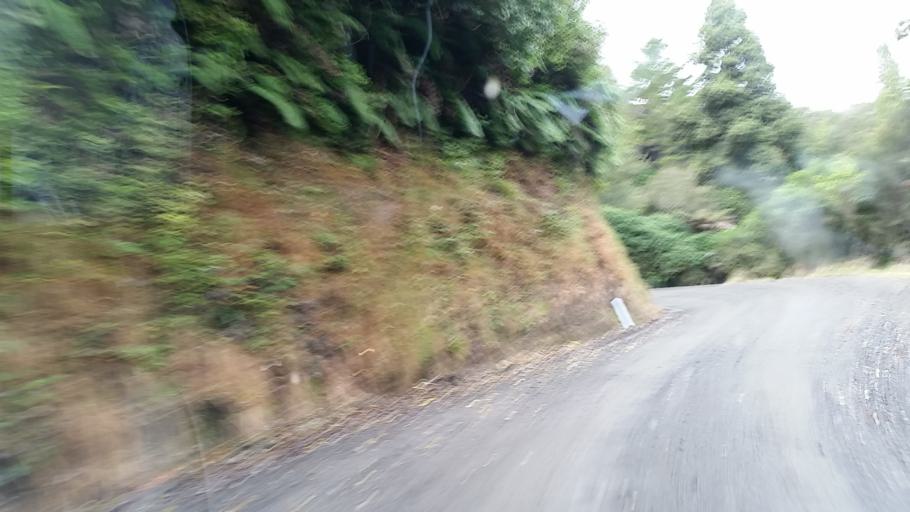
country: NZ
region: Taranaki
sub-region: New Plymouth District
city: Waitara
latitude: -39.1609
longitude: 174.5384
